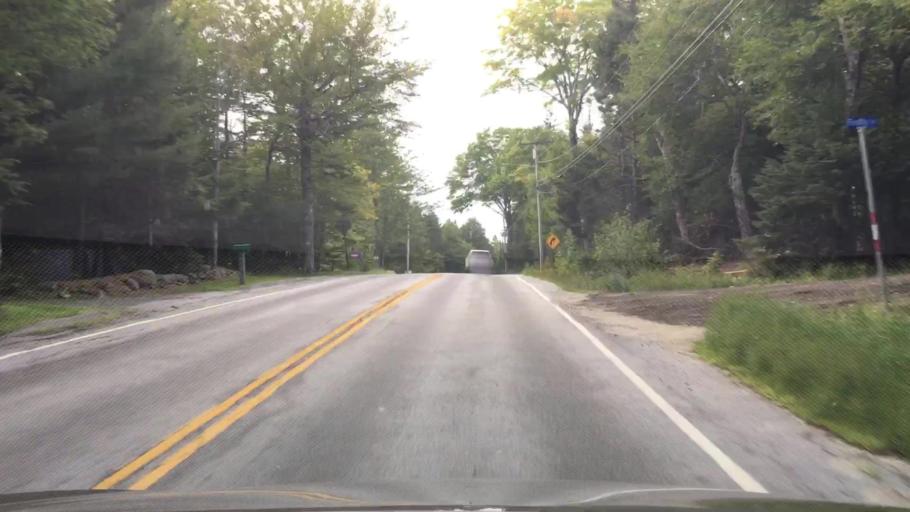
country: US
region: Maine
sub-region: Hancock County
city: Penobscot
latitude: 44.4268
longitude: -68.6016
